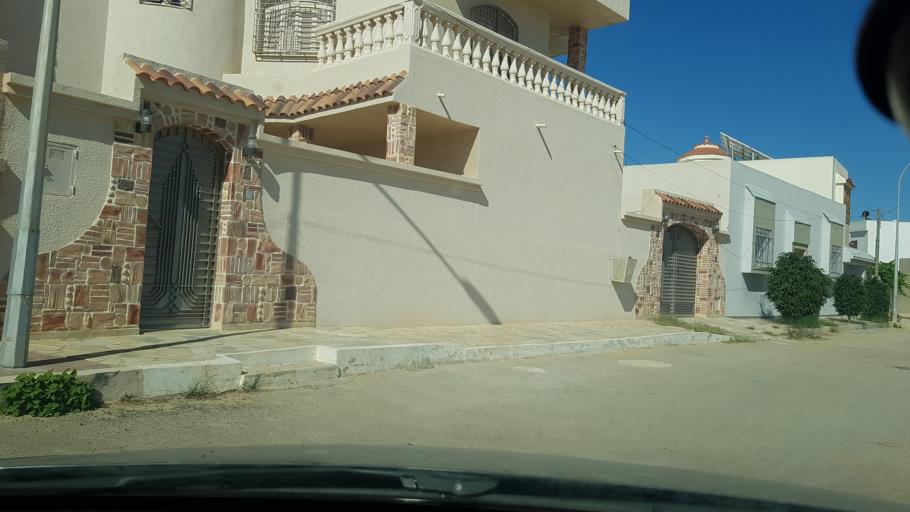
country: TN
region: Safaqis
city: Al Qarmadah
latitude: 34.8260
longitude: 10.7574
